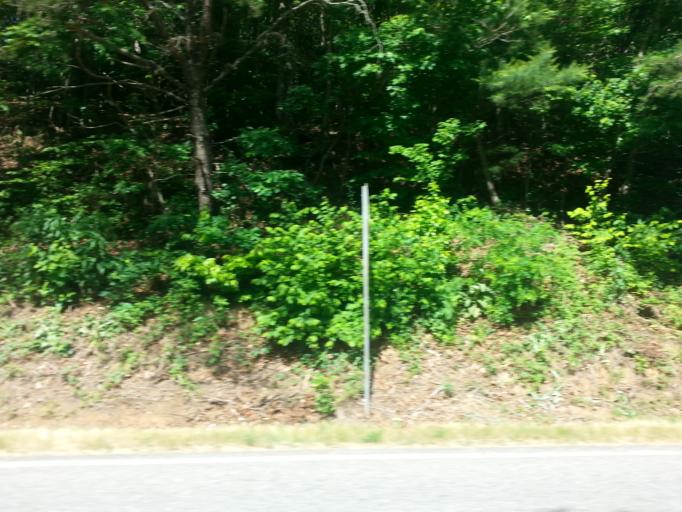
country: US
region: Georgia
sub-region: Towns County
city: Hiawassee
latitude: 34.8743
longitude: -83.7182
